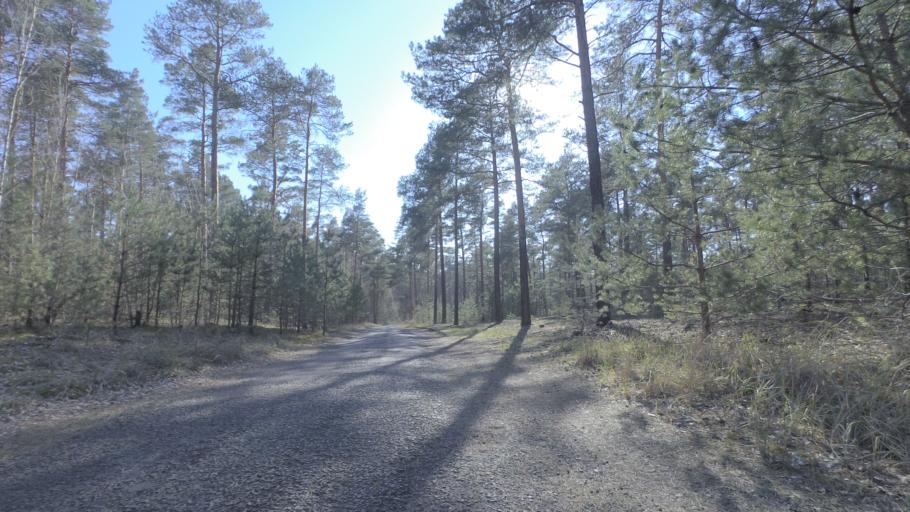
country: DE
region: Brandenburg
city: Teupitz
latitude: 52.1187
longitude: 13.5407
